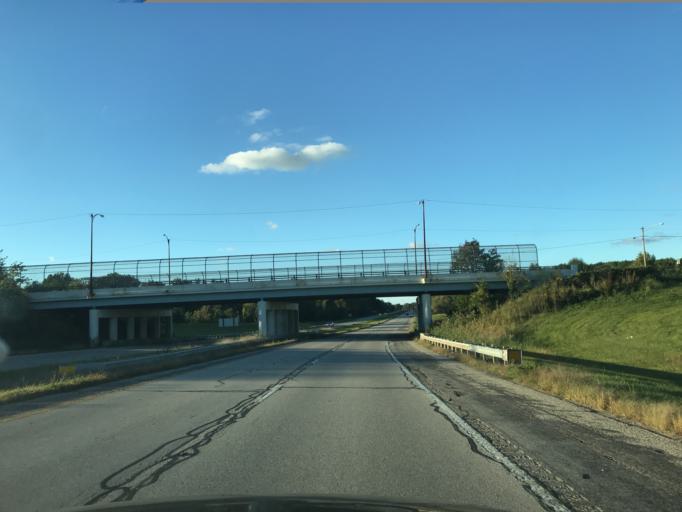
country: US
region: Ohio
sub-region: Ashtabula County
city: Edgewood
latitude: 41.8880
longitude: -80.7807
